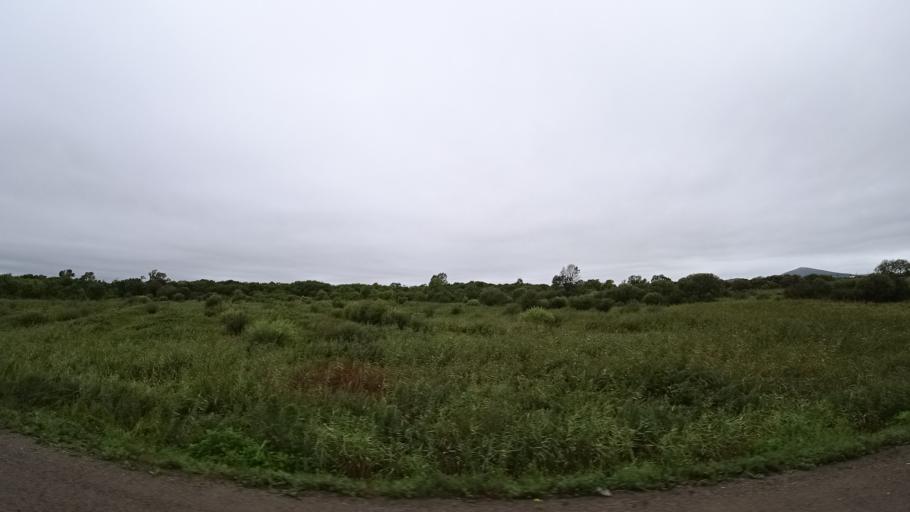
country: RU
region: Primorskiy
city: Monastyrishche
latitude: 44.2198
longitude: 132.4516
